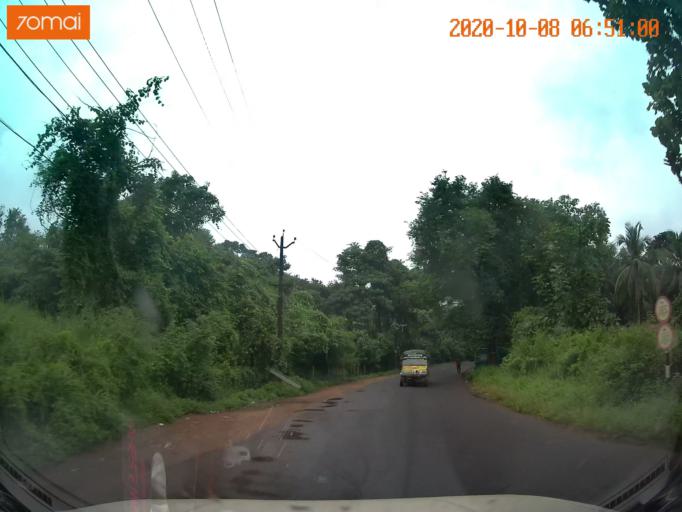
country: IN
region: Kerala
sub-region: Thrissur District
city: Kunnamkulam
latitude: 10.6881
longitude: 76.0970
